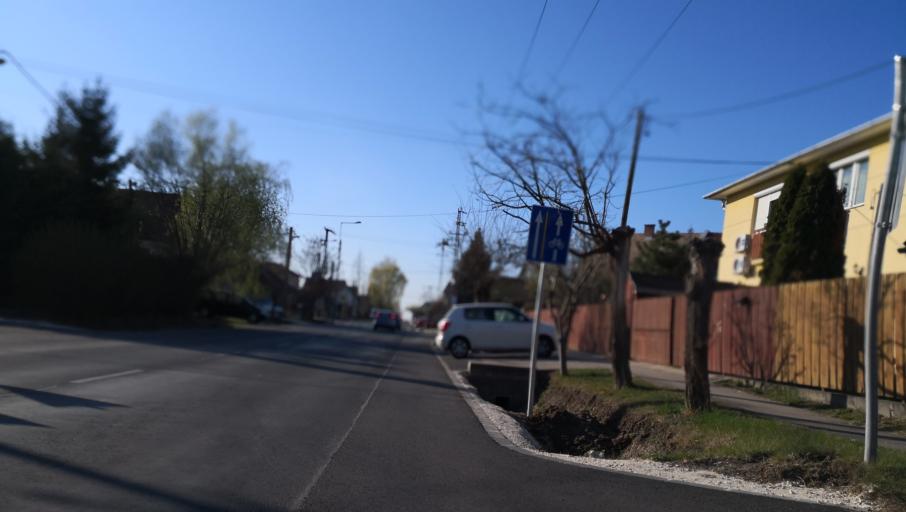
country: HU
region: Budapest
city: Budapest XVII. keruelet
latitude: 47.4984
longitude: 19.2704
